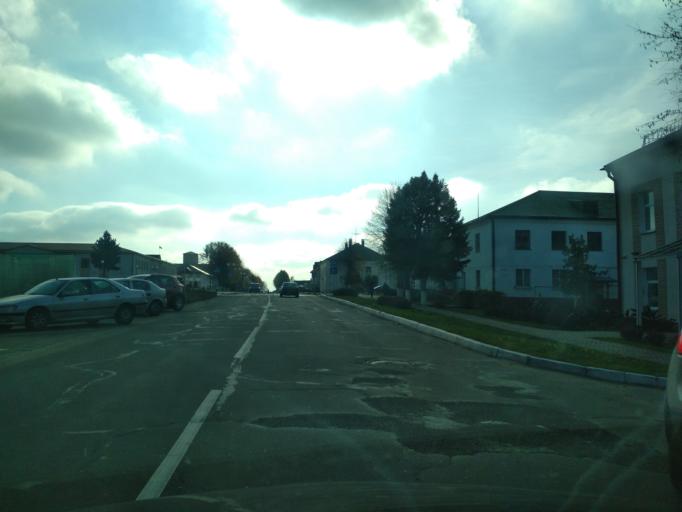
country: BY
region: Minsk
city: Mar''ina Horka
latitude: 53.5123
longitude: 28.1468
